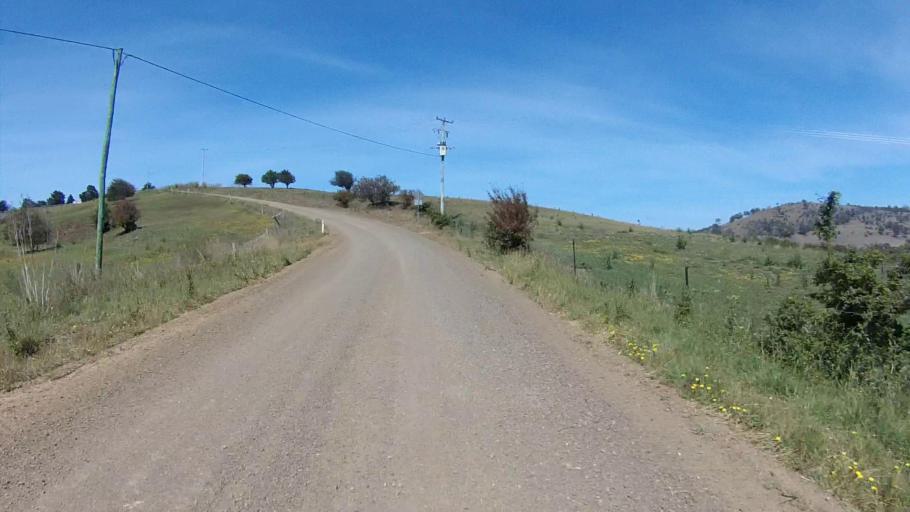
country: AU
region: Tasmania
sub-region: Sorell
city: Sorell
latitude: -42.7538
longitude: 147.6262
